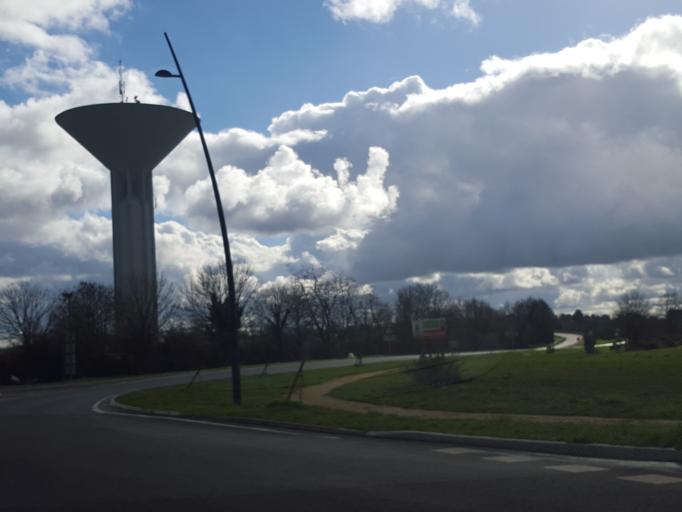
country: FR
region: Pays de la Loire
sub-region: Departement de la Vendee
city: Belleville-sur-Vie
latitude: 46.7745
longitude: -1.4312
